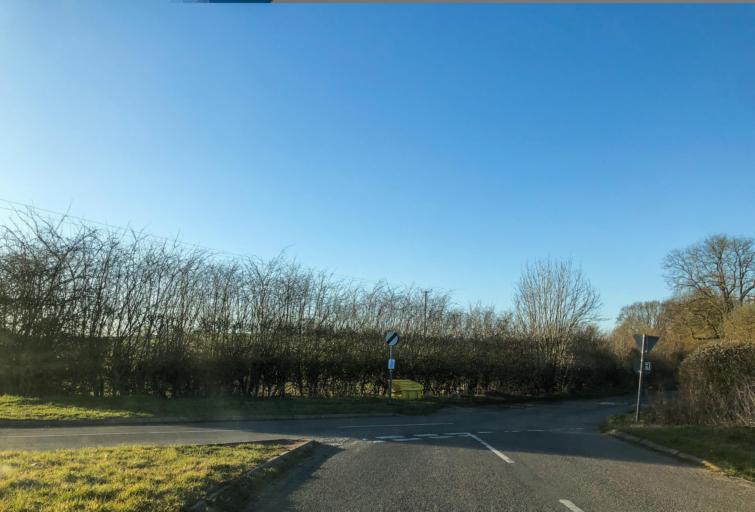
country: GB
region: England
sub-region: Warwickshire
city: Wroxall
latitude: 52.2739
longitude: -1.6641
